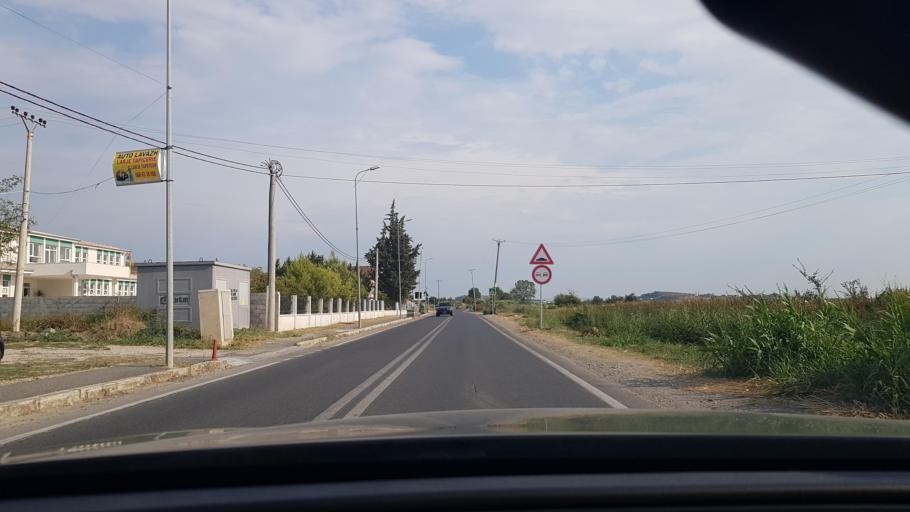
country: AL
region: Durres
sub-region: Rrethi i Durresit
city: Manze
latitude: 41.4620
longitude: 19.5639
